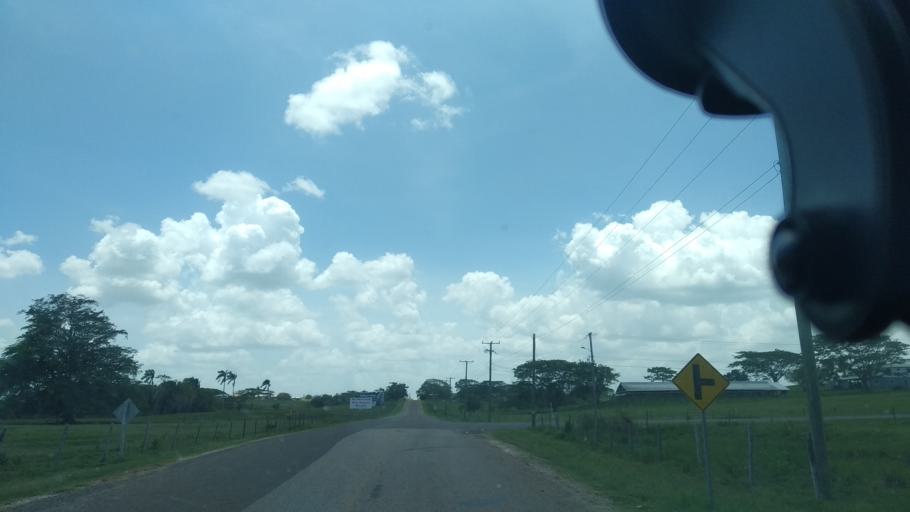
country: BZ
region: Cayo
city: San Ignacio
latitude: 17.2474
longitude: -88.9874
